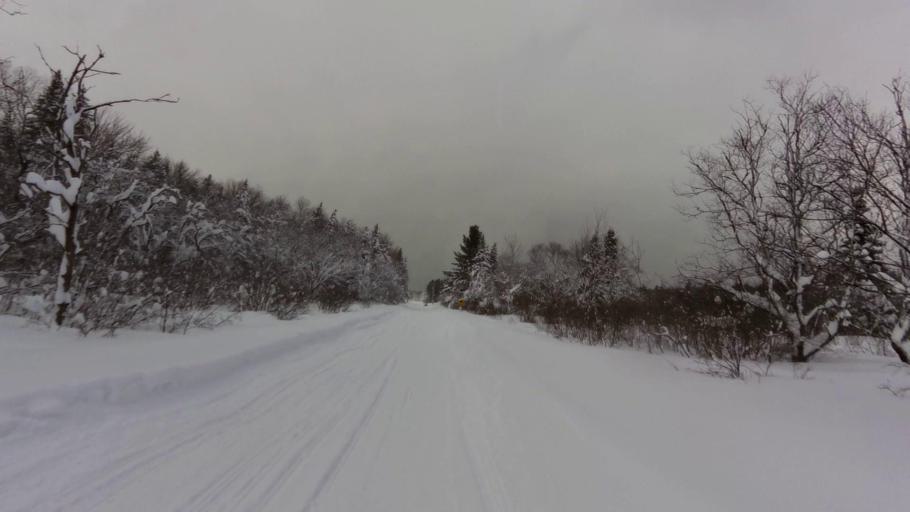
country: US
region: New York
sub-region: Lewis County
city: Lowville
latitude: 43.7529
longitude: -75.6757
